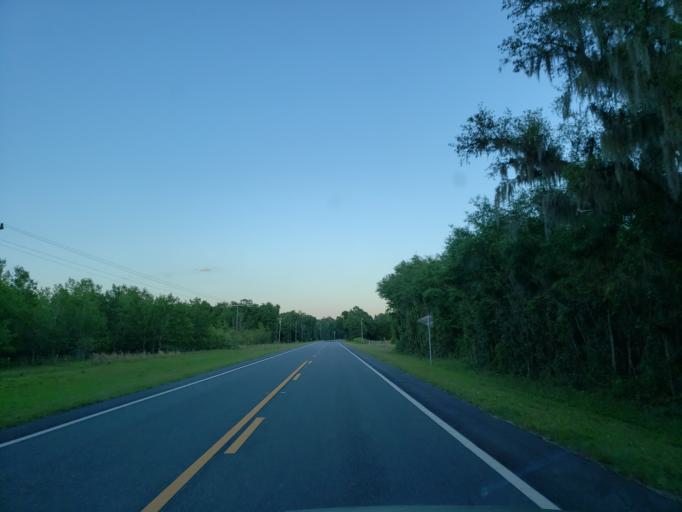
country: US
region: Georgia
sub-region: Echols County
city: Statenville
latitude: 30.5811
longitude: -83.1862
